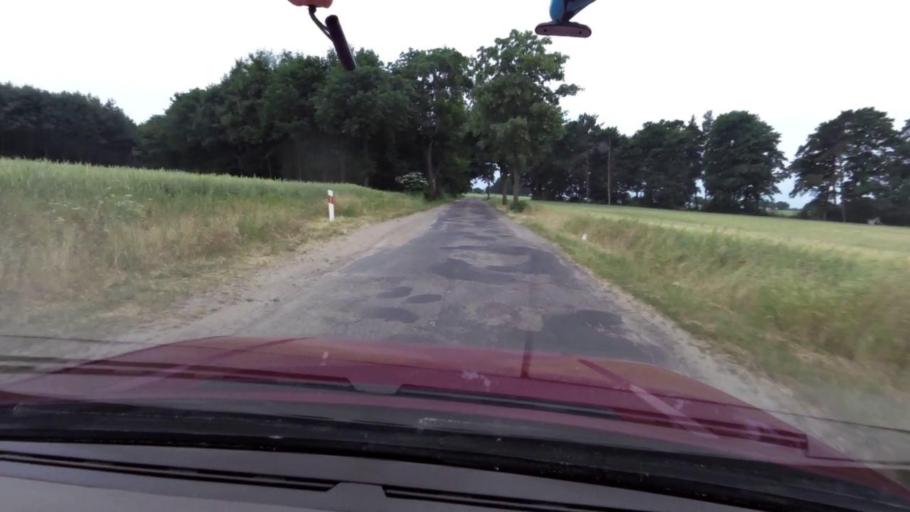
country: PL
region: Pomeranian Voivodeship
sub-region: Powiat slupski
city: Kepice
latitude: 54.2060
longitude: 16.8195
